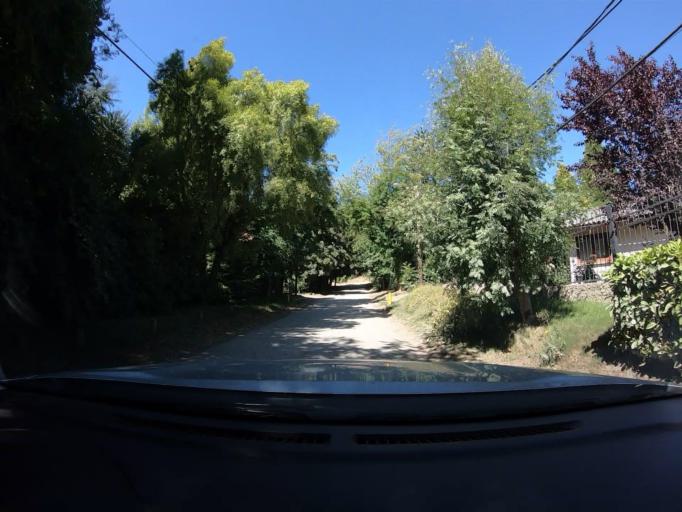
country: AR
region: Rio Negro
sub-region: Departamento de Bariloche
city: San Carlos de Bariloche
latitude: -41.1232
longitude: -71.3926
